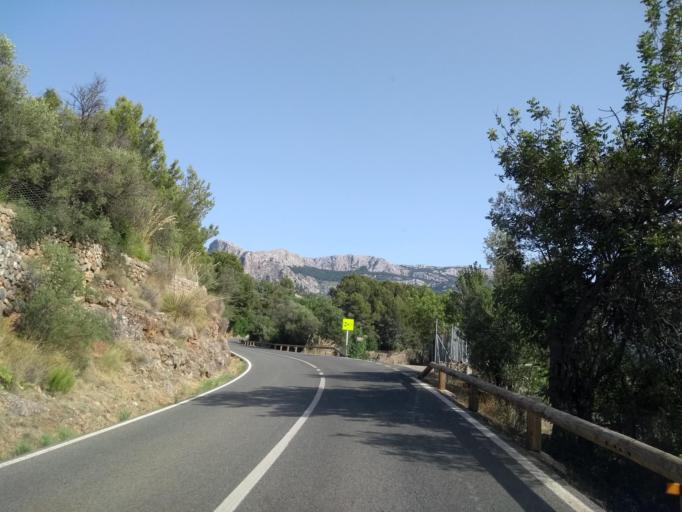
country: ES
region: Balearic Islands
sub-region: Illes Balears
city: Soller
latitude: 39.7819
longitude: 2.7167
